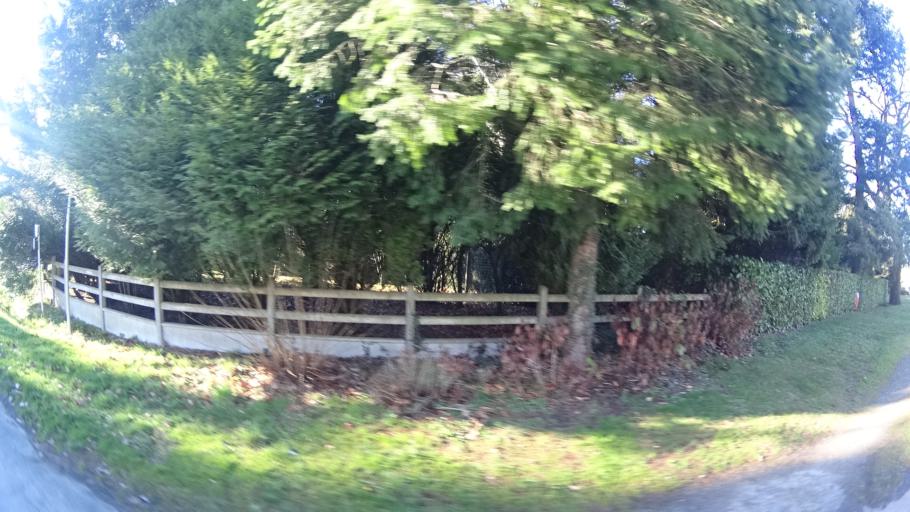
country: FR
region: Brittany
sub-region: Departement du Morbihan
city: Allaire
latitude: 47.6400
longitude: -2.1650
